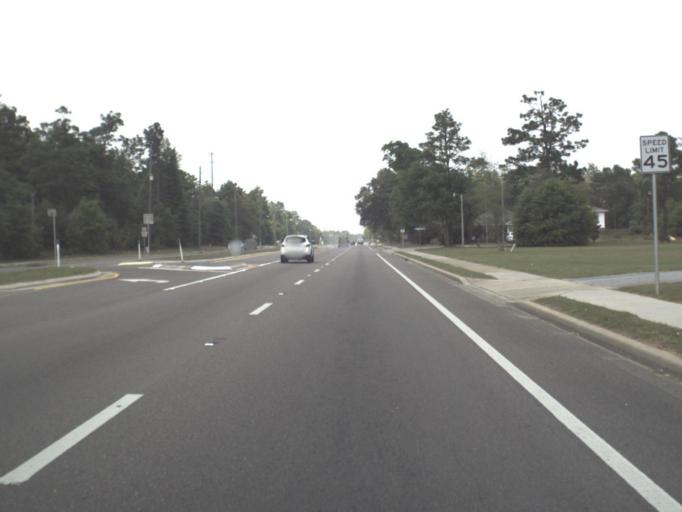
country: US
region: Florida
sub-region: Santa Rosa County
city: Milton
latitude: 30.6469
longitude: -87.0552
